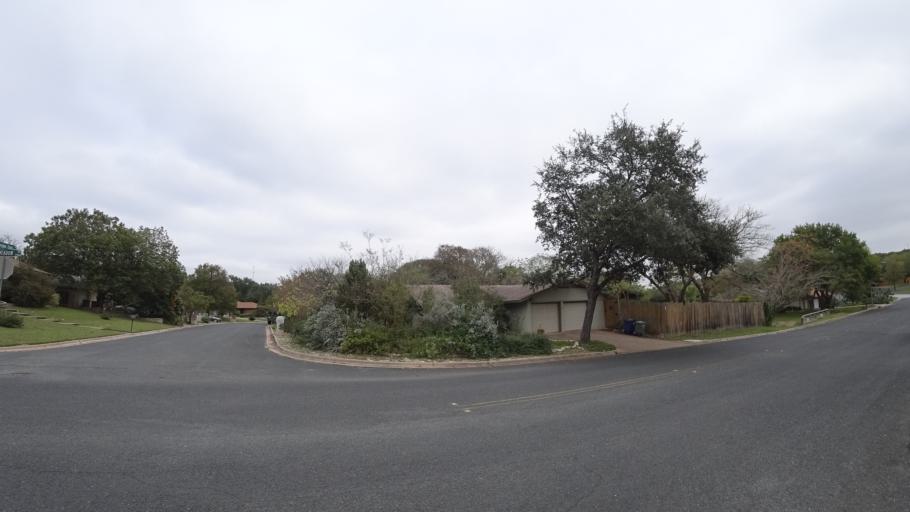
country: US
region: Texas
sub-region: Travis County
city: Barton Creek
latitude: 30.2361
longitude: -97.8822
